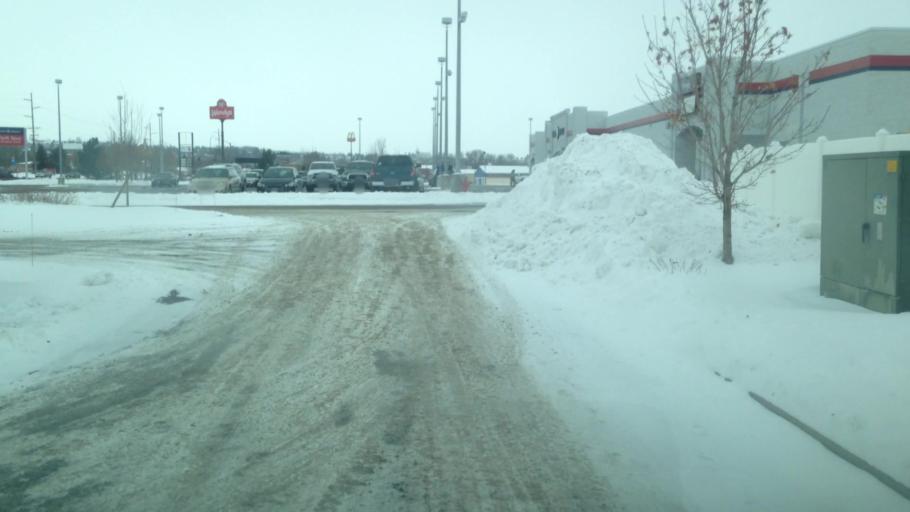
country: US
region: Idaho
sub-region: Madison County
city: Rexburg
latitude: 43.8397
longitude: -111.7789
